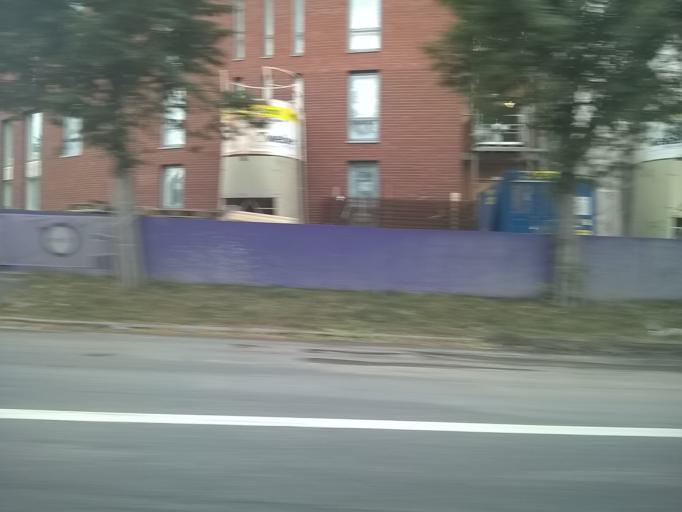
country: FI
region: Pirkanmaa
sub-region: Tampere
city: Tampere
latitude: 61.5067
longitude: 23.7834
